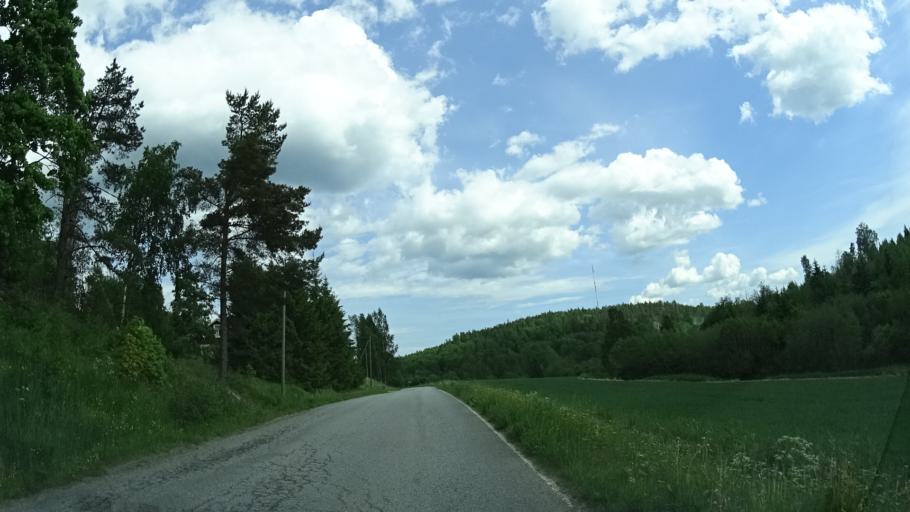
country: FI
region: Uusimaa
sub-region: Helsinki
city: Siuntio
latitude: 60.1970
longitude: 24.2266
